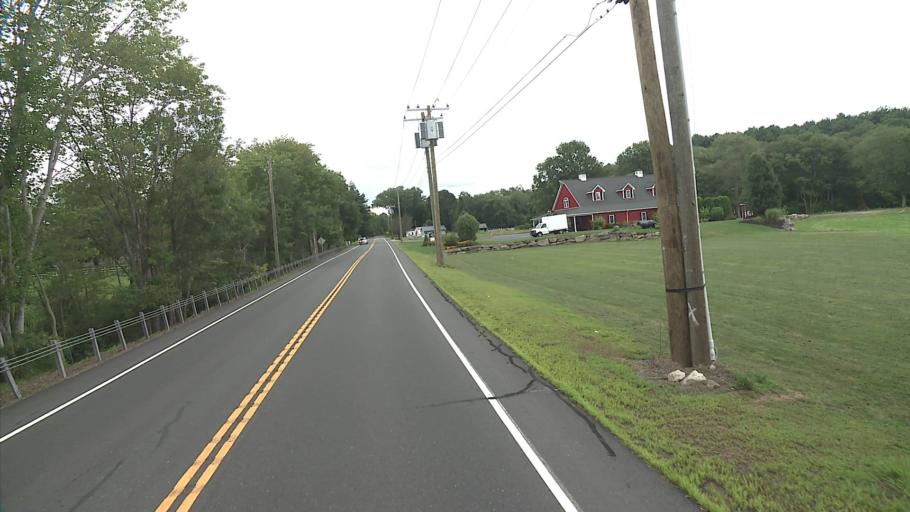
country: US
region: Connecticut
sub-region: Tolland County
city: Tolland
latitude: 41.8812
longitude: -72.3496
